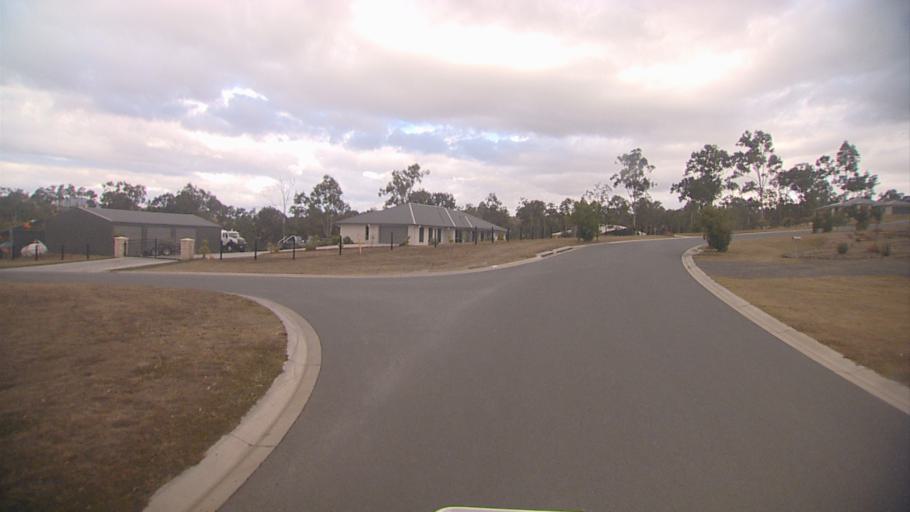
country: AU
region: Queensland
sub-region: Logan
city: Cedar Vale
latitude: -27.8623
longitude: 153.0788
